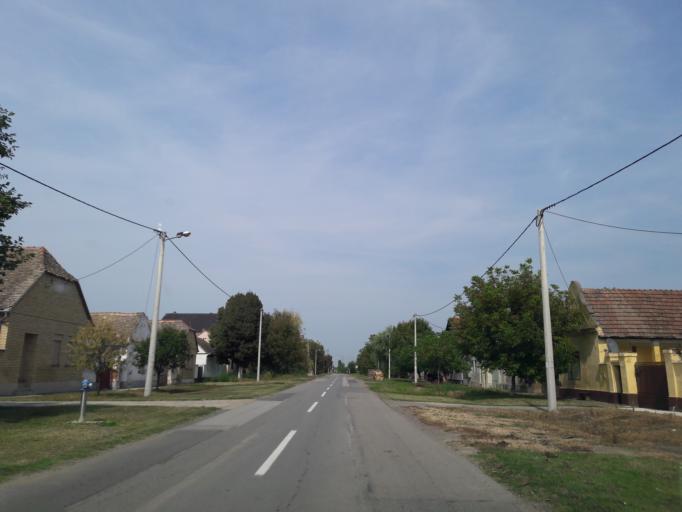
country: HR
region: Vukovarsko-Srijemska
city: Nustar
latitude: 45.3741
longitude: 18.8494
